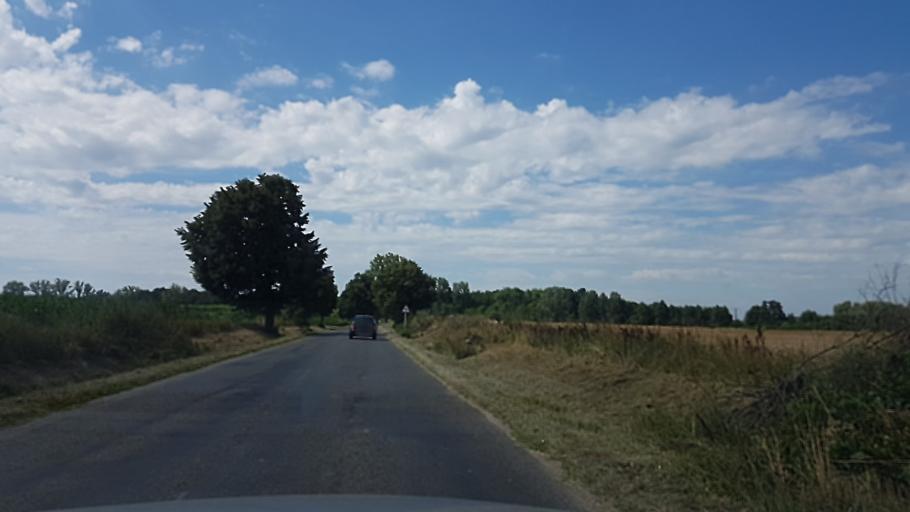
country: HU
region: Somogy
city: Barcs
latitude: 45.9569
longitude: 17.5981
